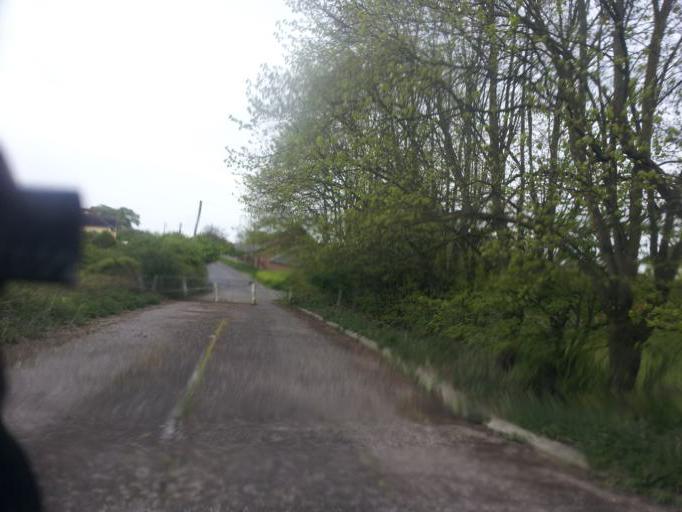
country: GB
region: England
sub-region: Medway
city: High Halstow
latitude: 51.4394
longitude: 0.5734
